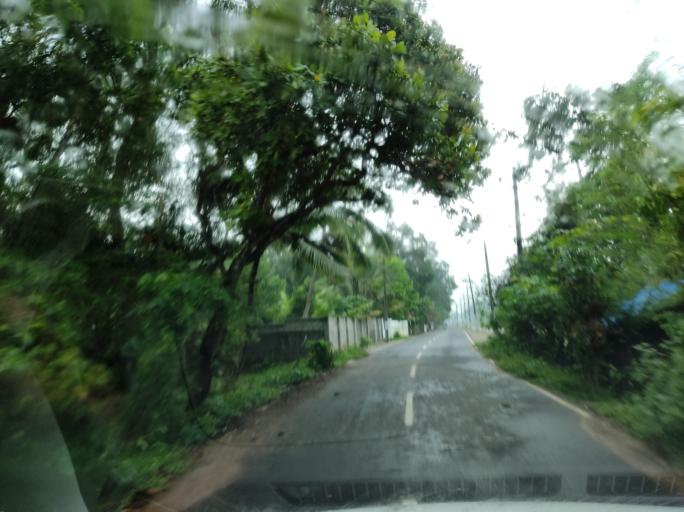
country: IN
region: Kerala
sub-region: Alappuzha
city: Alleppey
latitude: 9.5638
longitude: 76.3302
